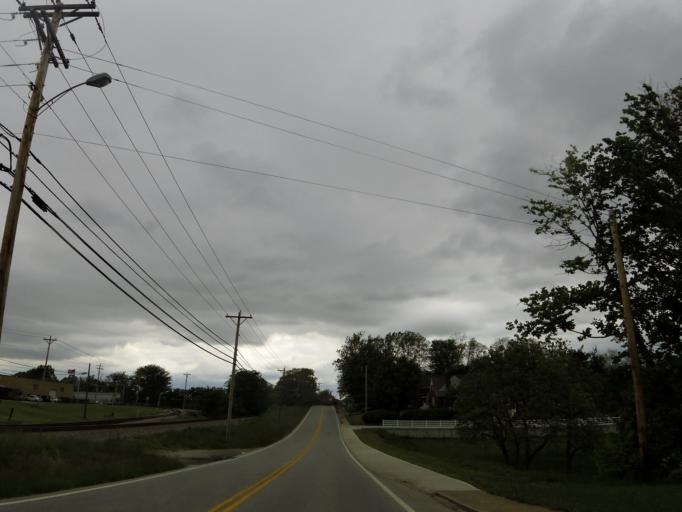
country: US
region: Kentucky
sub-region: Grant County
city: Williamstown
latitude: 38.6487
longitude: -84.5659
